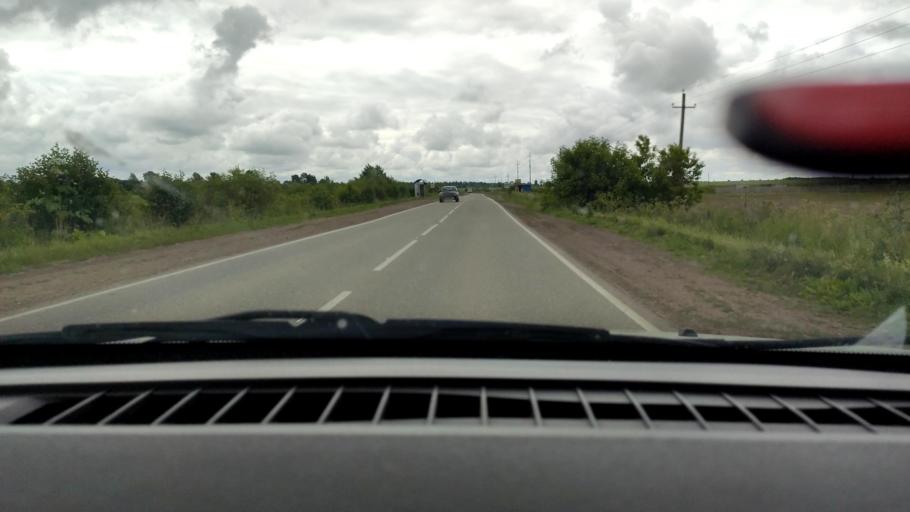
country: RU
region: Perm
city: Chaykovskaya
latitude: 58.0810
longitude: 55.6165
